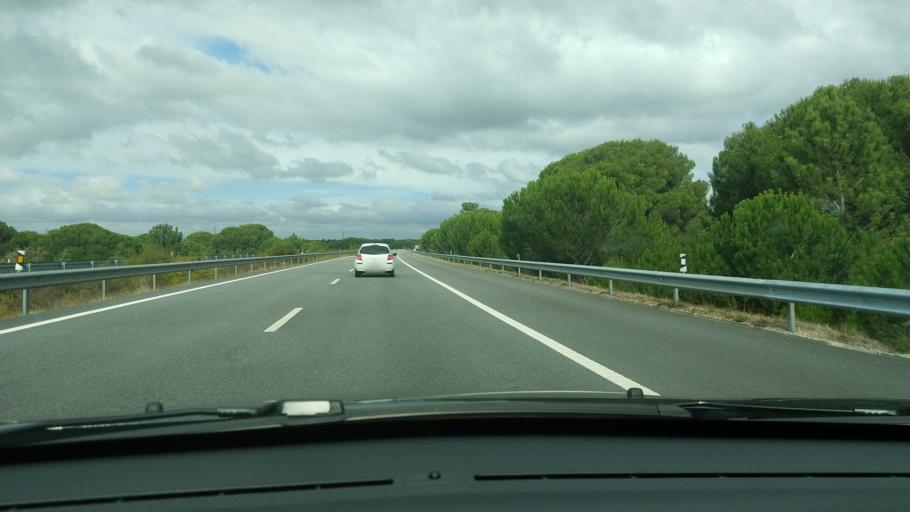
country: PT
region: Evora
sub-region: Vendas Novas
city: Vendas Novas
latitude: 38.5499
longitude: -8.6139
